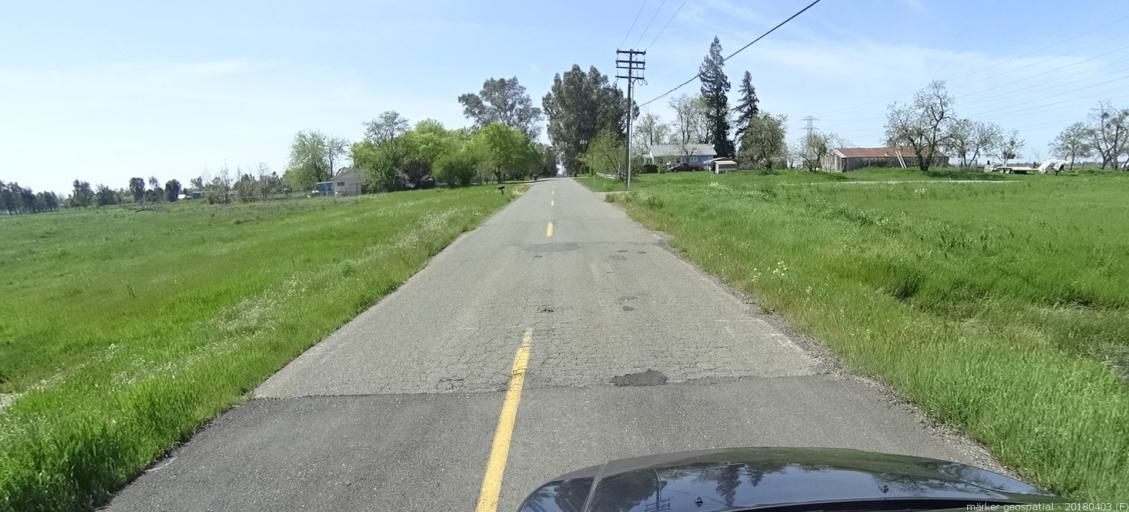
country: US
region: California
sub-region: Sacramento County
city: Herald
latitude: 38.3507
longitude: -121.2346
